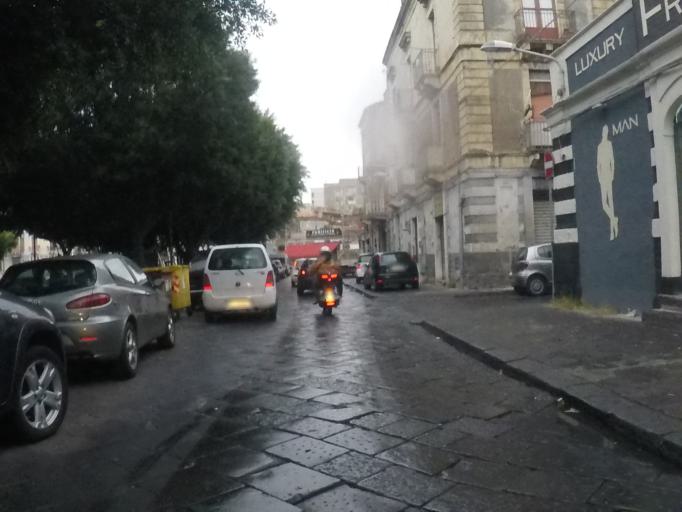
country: IT
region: Sicily
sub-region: Catania
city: Catania
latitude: 37.4999
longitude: 15.0733
